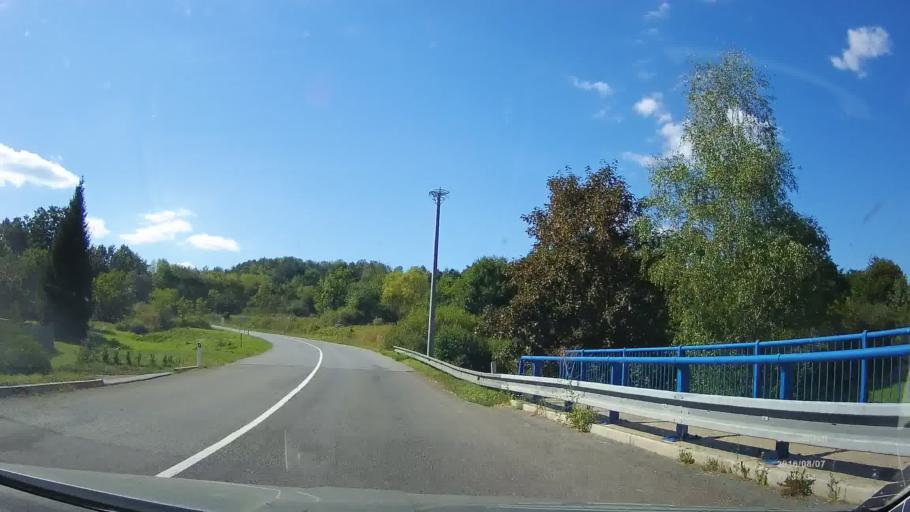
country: SK
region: Presovsky
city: Giraltovce
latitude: 49.1188
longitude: 21.6031
